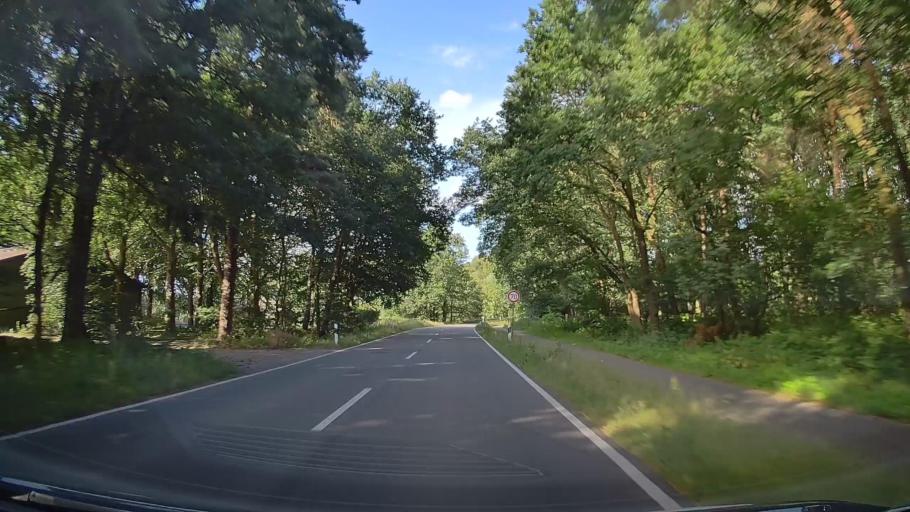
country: DE
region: Lower Saxony
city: Bosel
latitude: 52.9598
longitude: 7.9073
